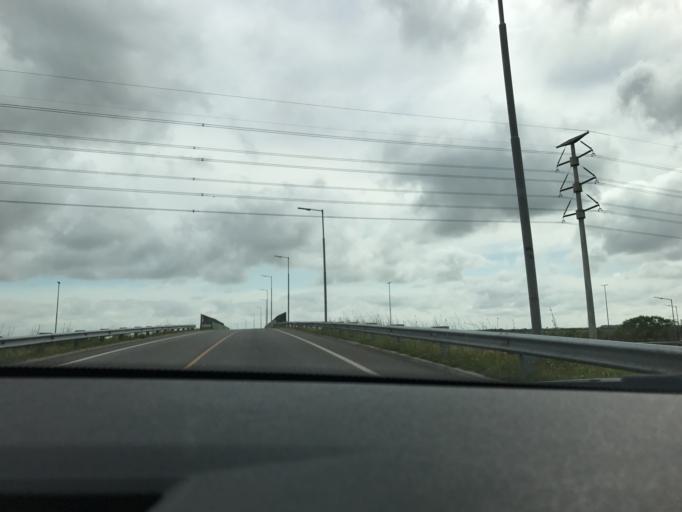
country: AR
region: Buenos Aires
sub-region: Partido de La Plata
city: La Plata
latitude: -34.8398
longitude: -58.0708
